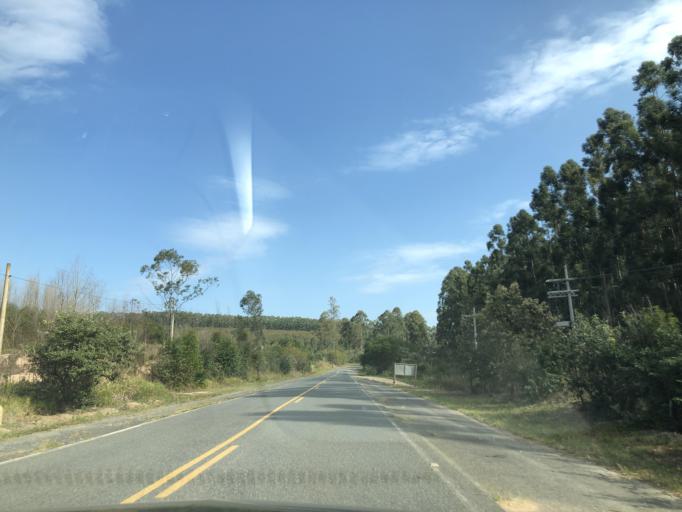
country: BR
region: Sao Paulo
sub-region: Pilar Do Sul
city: Pilar do Sul
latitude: -23.8128
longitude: -47.6457
